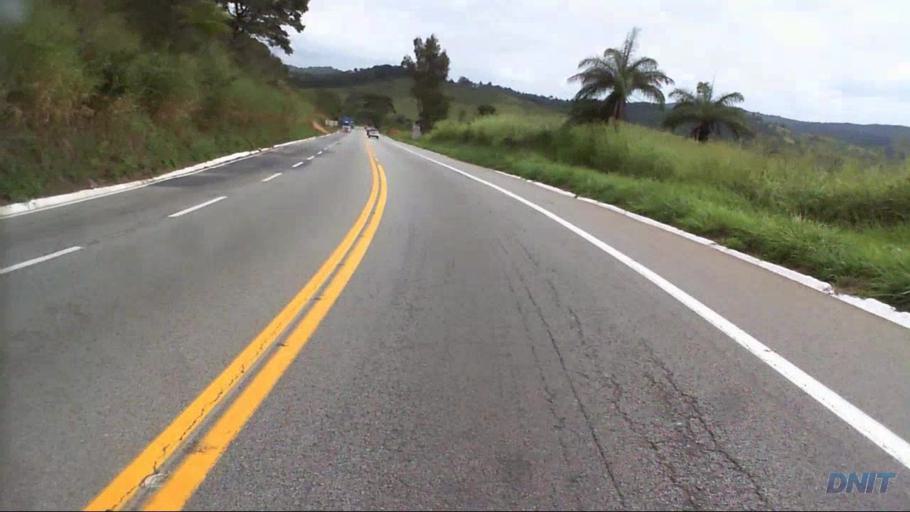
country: BR
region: Minas Gerais
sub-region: Caete
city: Caete
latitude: -19.7406
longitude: -43.6086
